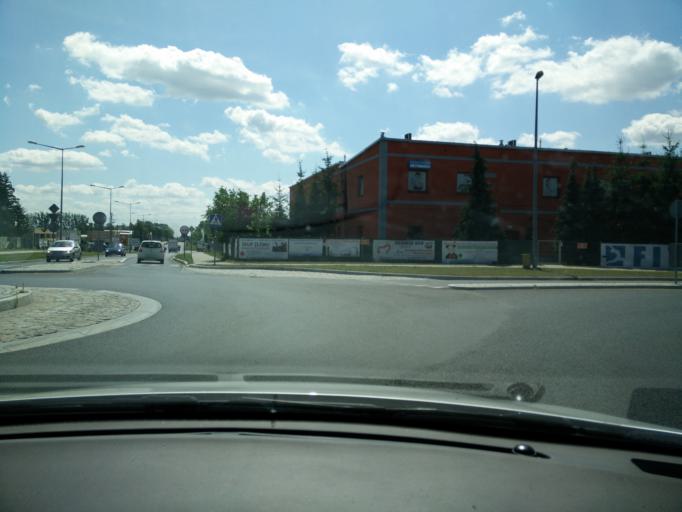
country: PL
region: Greater Poland Voivodeship
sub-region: Powiat sredzki
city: Sroda Wielkopolska
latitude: 52.2220
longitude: 17.2867
